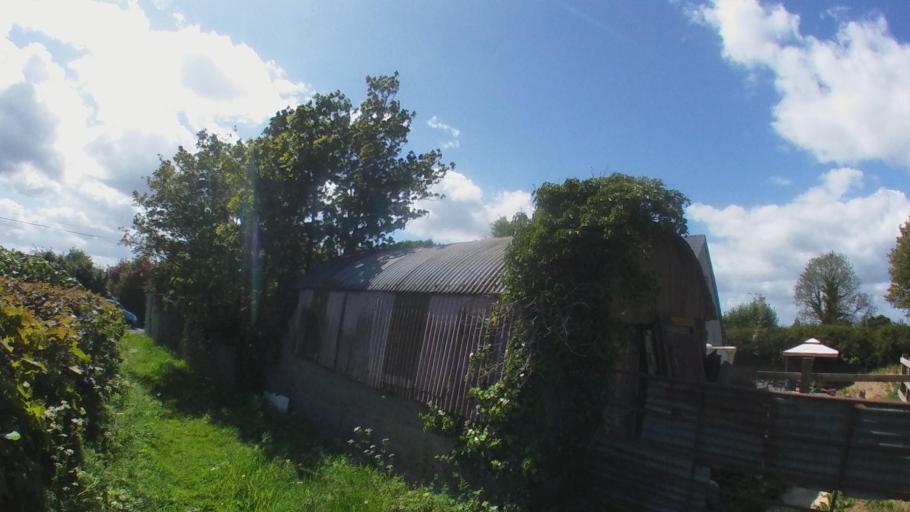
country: IE
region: Leinster
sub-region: Kilkenny
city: Thomastown
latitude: 52.5964
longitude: -7.1629
